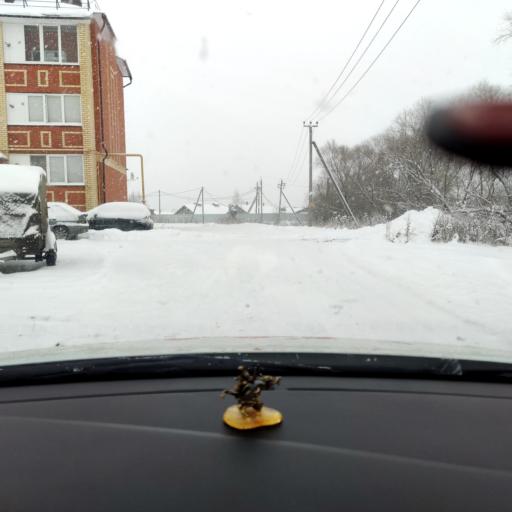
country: RU
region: Tatarstan
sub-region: Arskiy Rayon
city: Arsk
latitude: 56.0985
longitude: 49.8791
